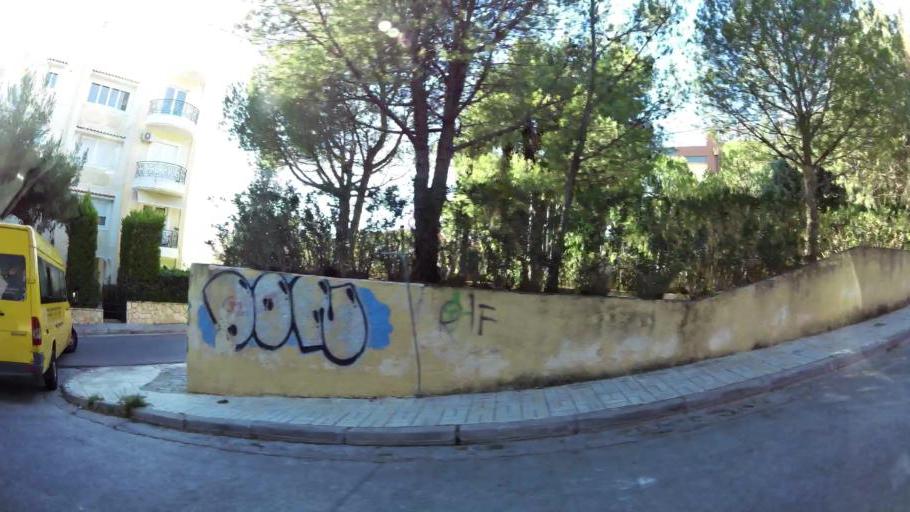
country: GR
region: Attica
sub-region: Nomarchia Athinas
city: Melissia
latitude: 38.0456
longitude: 23.8490
